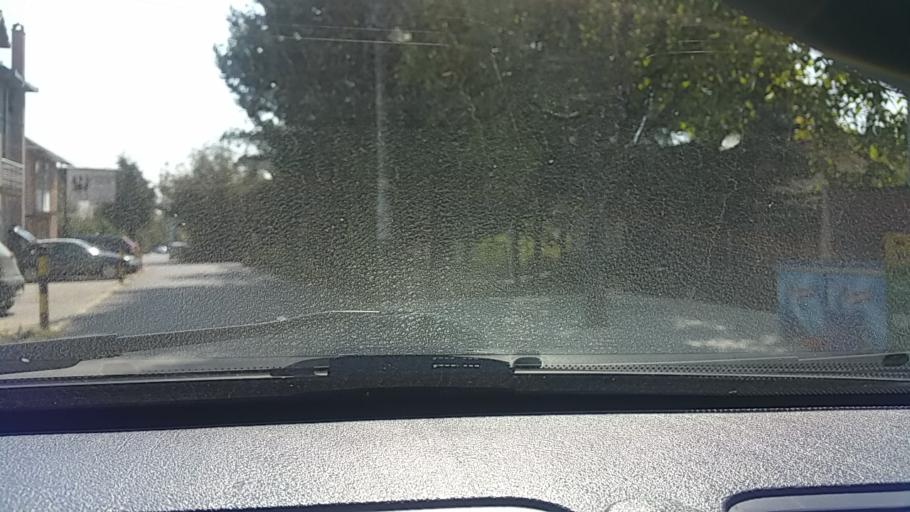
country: RS
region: Central Serbia
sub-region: Belgrade
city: Rakovica
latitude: 44.7375
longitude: 20.4634
